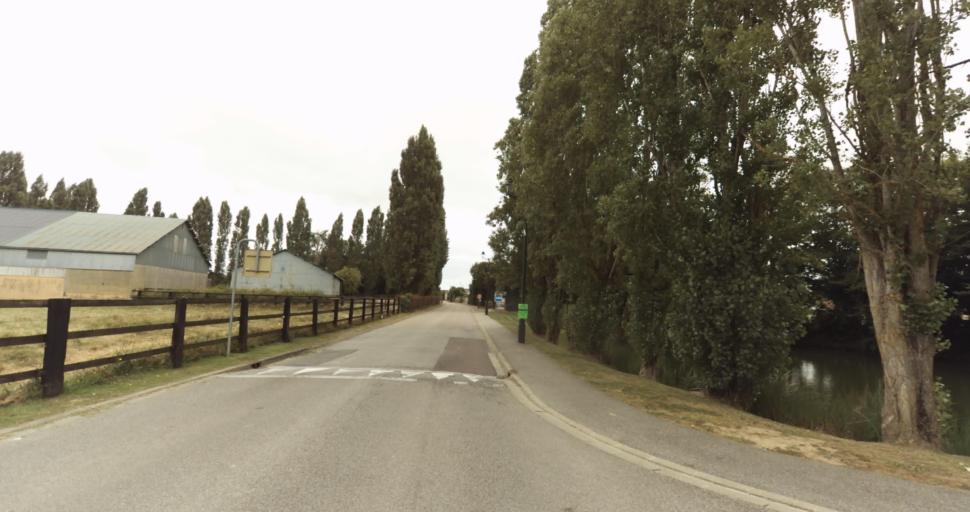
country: FR
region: Haute-Normandie
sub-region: Departement de l'Eure
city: Gravigny
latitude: 49.0369
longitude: 1.2041
